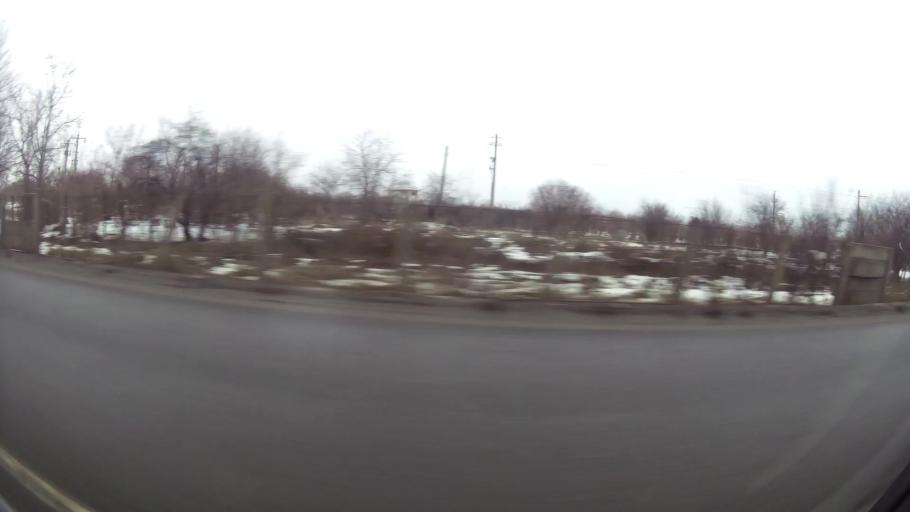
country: RO
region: Ilfov
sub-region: Comuna Bragadiru
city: Bragadiru
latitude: 44.3844
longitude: 25.9915
